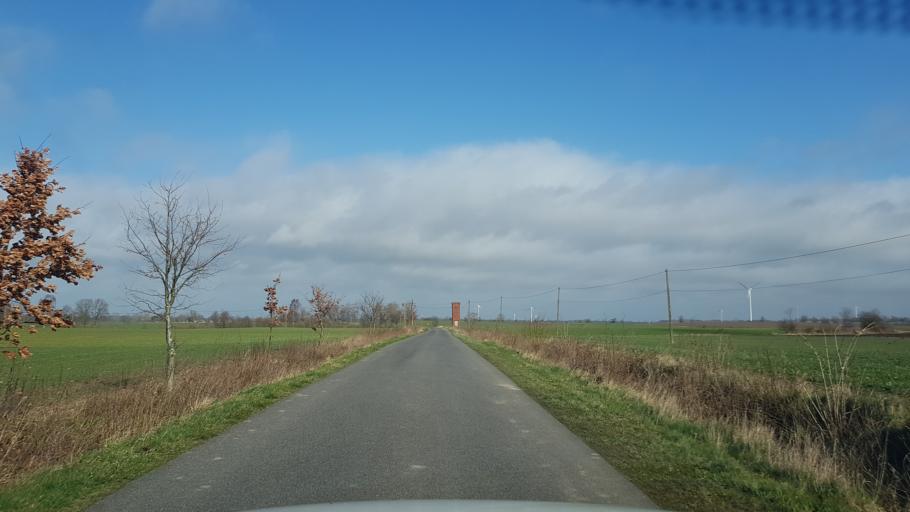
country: PL
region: West Pomeranian Voivodeship
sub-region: Powiat slawienski
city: Slawno
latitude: 54.4946
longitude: 16.6498
